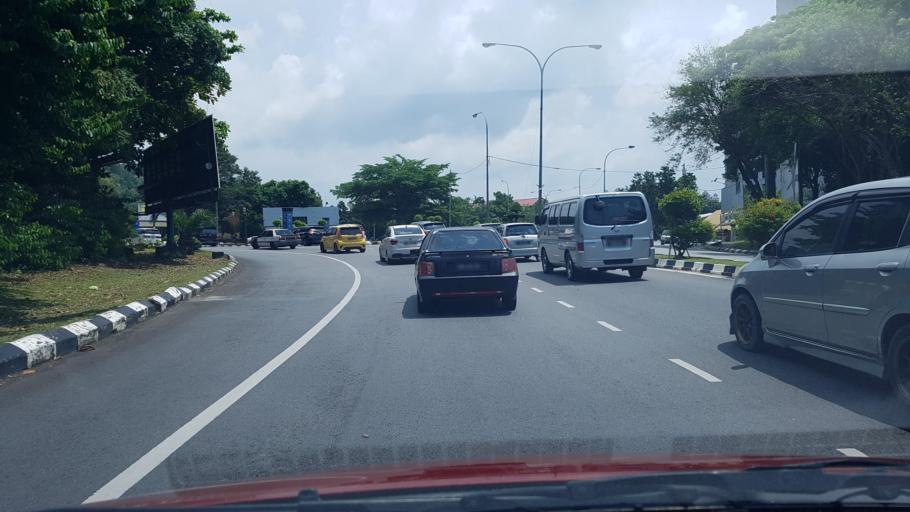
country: MY
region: Terengganu
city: Kuala Terengganu
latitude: 5.3201
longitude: 103.1429
